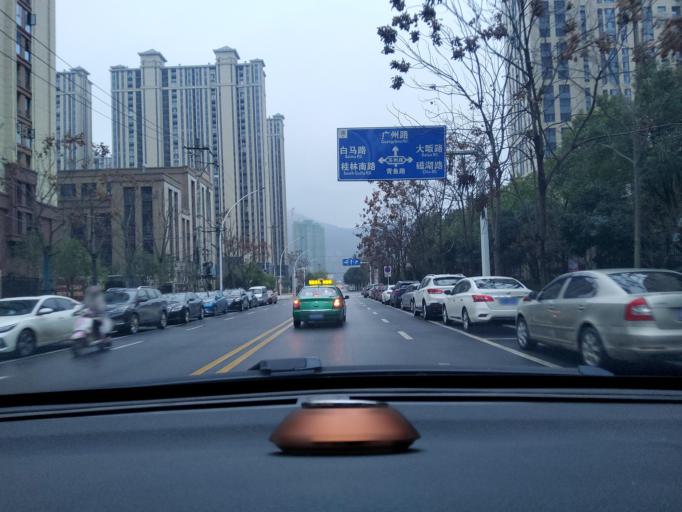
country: CN
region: Hubei
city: Tuanchengshan
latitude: 30.1967
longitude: 115.0094
